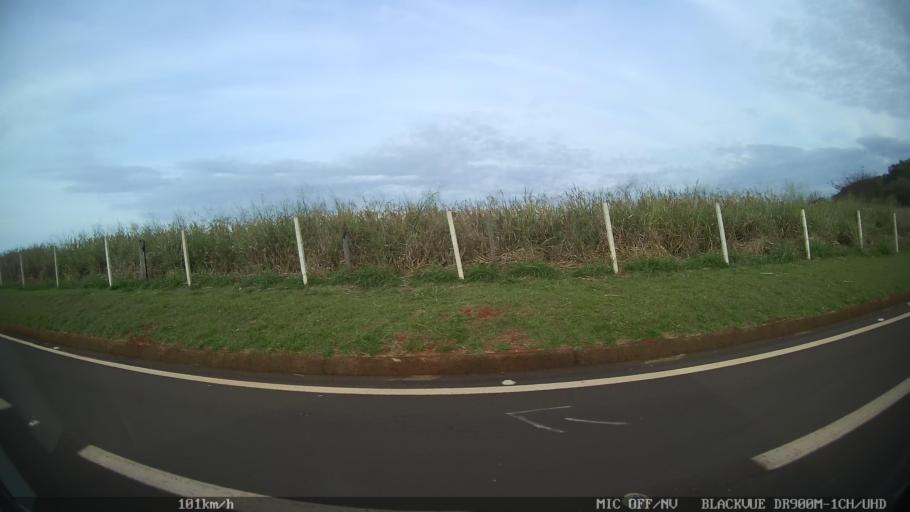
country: BR
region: Sao Paulo
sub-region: Iracemapolis
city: Iracemapolis
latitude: -22.6365
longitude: -47.5079
